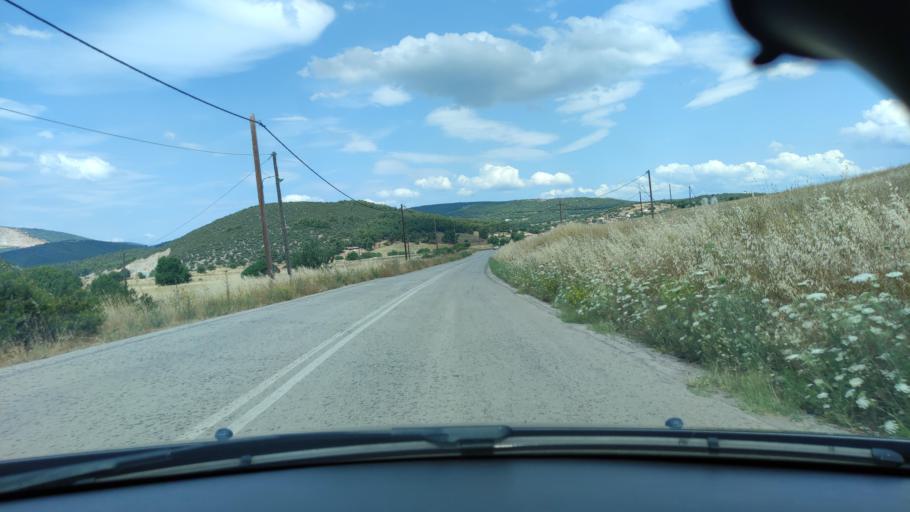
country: GR
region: Central Greece
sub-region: Nomos Evvoias
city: Afration
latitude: 38.5202
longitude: 23.7319
